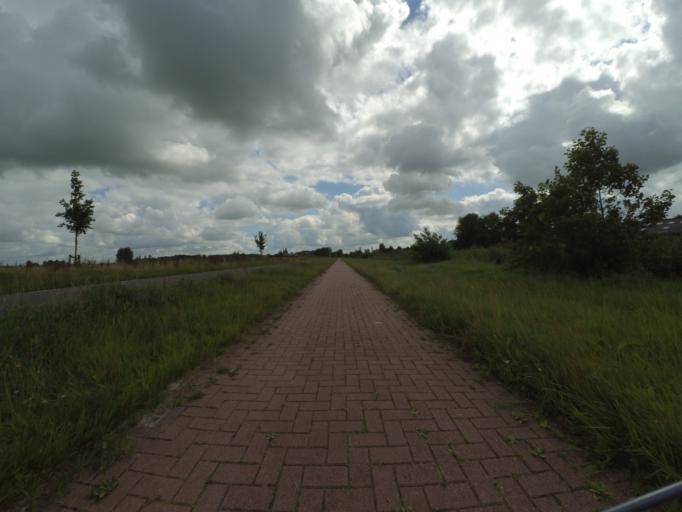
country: NL
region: Friesland
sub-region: Gemeente Achtkarspelen
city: Buitenpost
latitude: 53.2566
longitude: 6.1533
